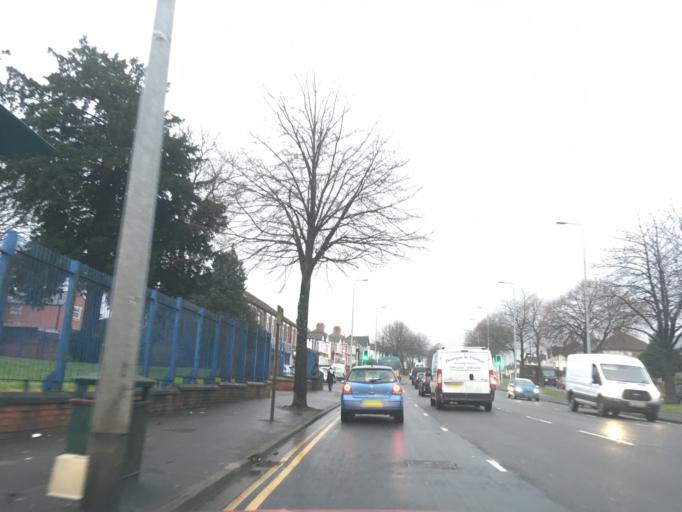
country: GB
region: Wales
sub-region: Cardiff
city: Radyr
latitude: 51.4789
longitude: -3.2405
